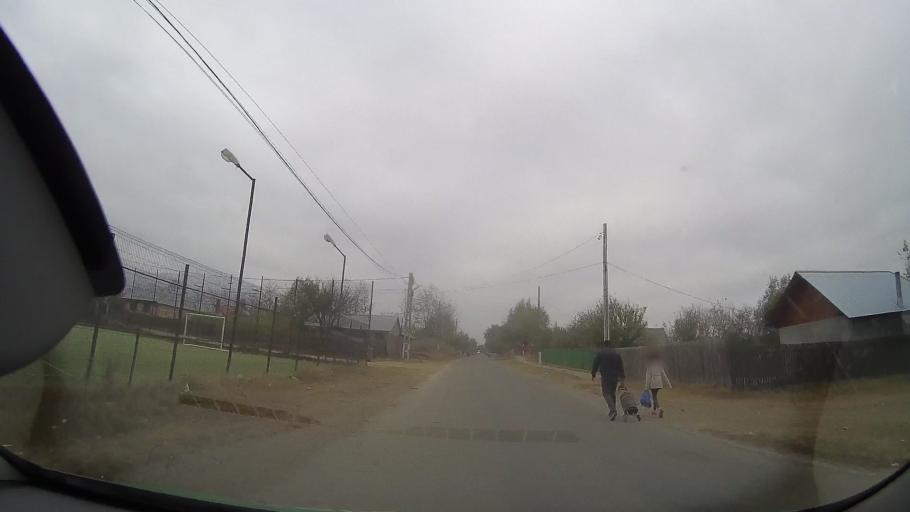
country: RO
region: Buzau
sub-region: Comuna Luciu
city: Luciu
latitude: 44.9683
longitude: 27.0923
